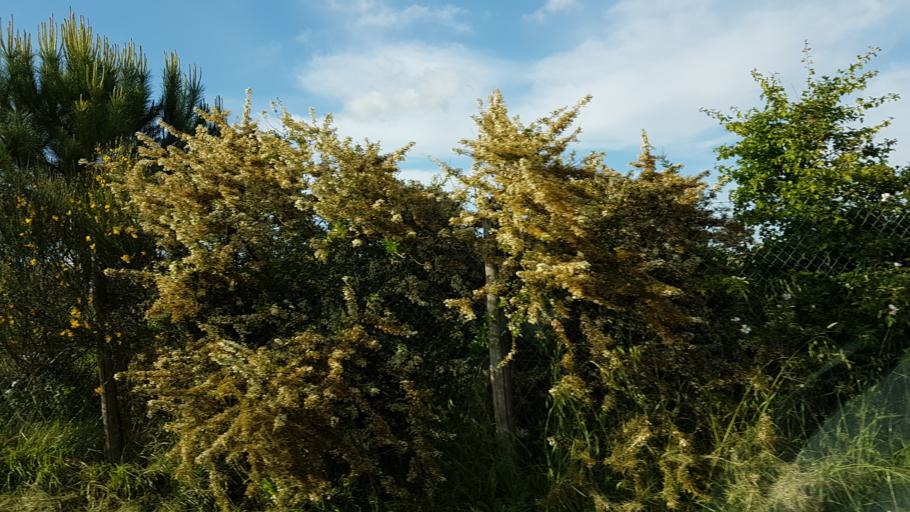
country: IT
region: Tuscany
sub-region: Province of Pisa
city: Chianni
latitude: 43.4815
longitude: 10.6779
